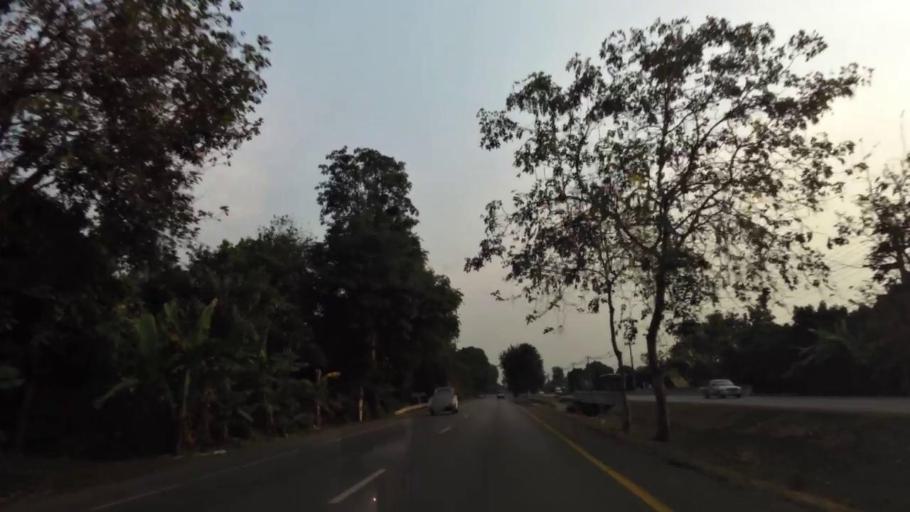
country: TH
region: Chanthaburi
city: Khlung
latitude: 12.4915
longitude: 102.1738
